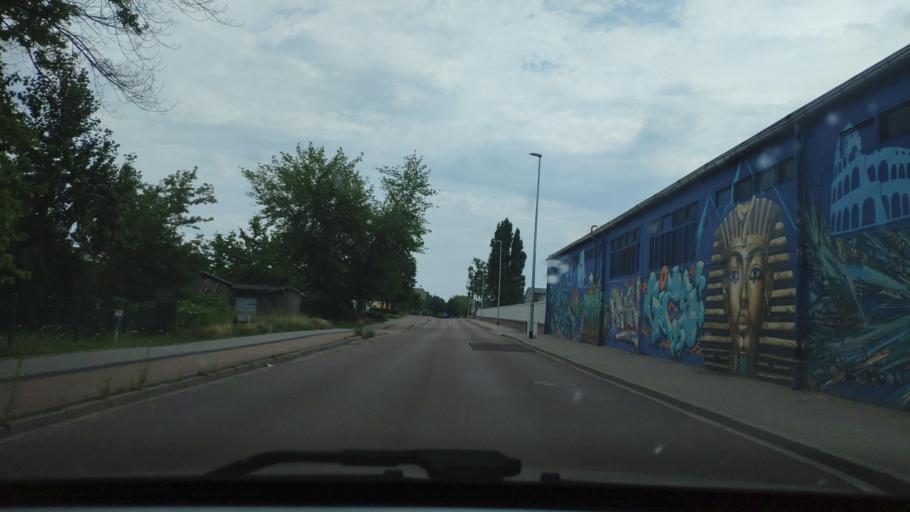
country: DE
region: Saxony-Anhalt
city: Bernburg
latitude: 51.7825
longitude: 11.7507
